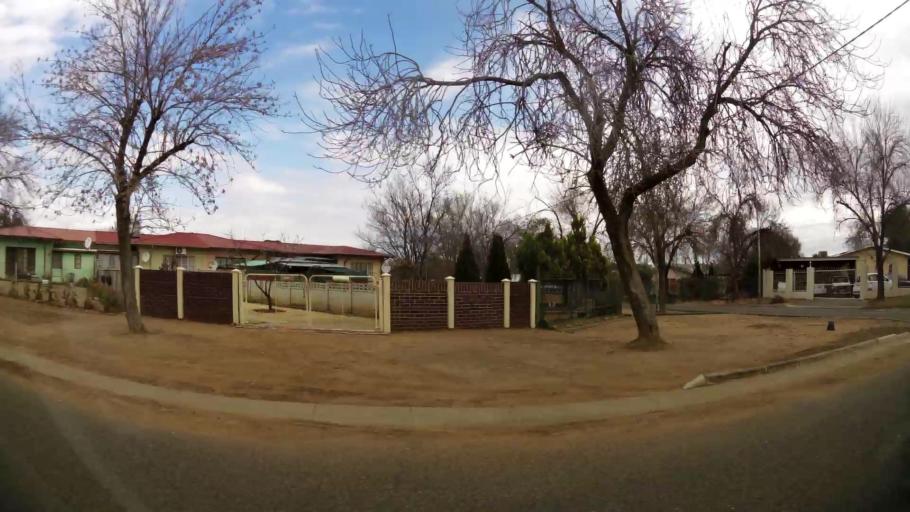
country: ZA
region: Orange Free State
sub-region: Fezile Dabi District Municipality
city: Kroonstad
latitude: -27.6406
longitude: 27.2291
